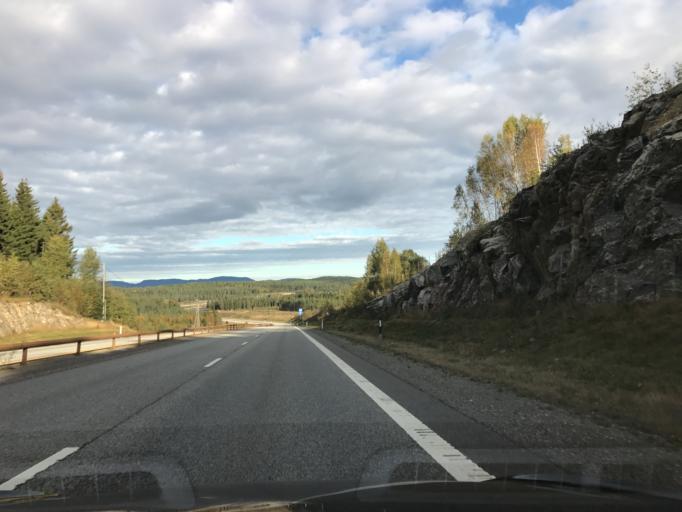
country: NO
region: Akershus
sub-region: Eidsvoll
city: Raholt
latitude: 60.2761
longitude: 11.1495
